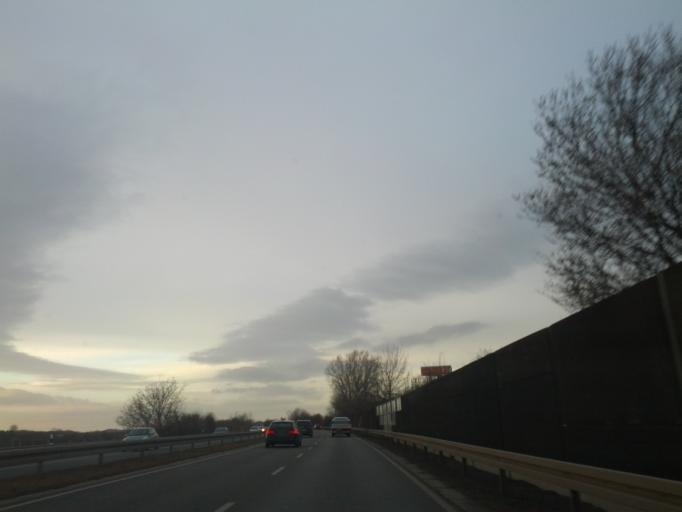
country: DE
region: Thuringia
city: Erfurt
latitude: 50.9995
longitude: 10.9999
